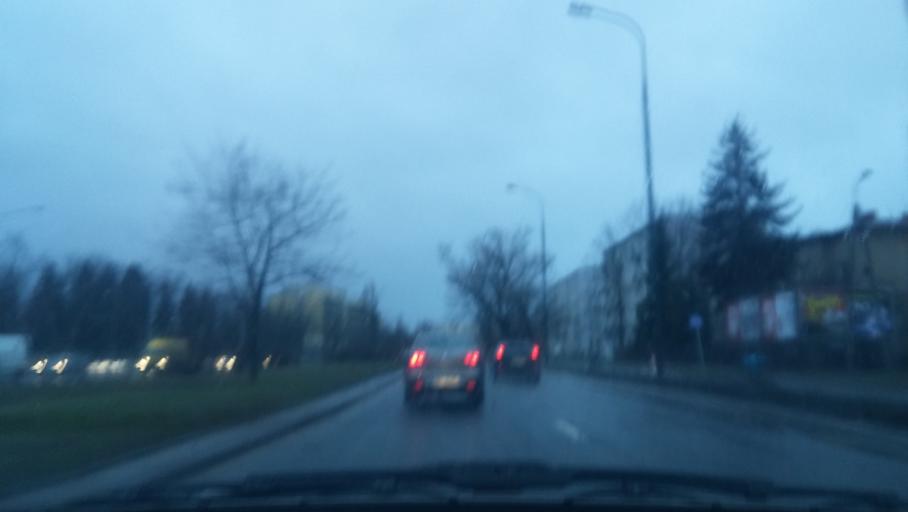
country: PL
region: Masovian Voivodeship
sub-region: Warszawa
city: Praga Poludnie
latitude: 52.2351
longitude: 21.0955
